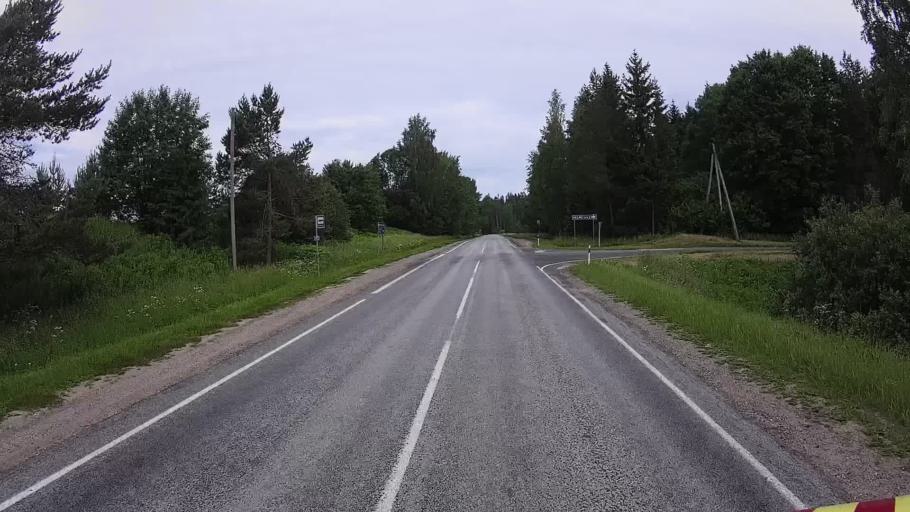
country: EE
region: Viljandimaa
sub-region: Karksi vald
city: Karksi-Nuia
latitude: 58.2148
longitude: 25.6199
